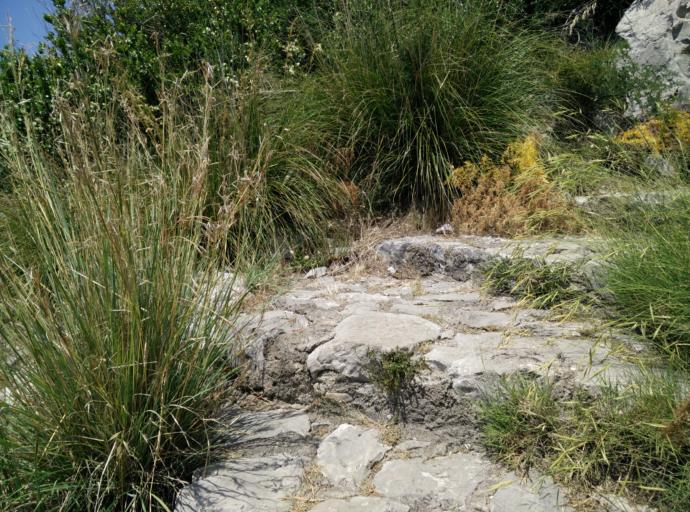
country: IT
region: Campania
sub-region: Provincia di Napoli
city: Massa Lubrense
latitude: 40.5944
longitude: 14.3799
